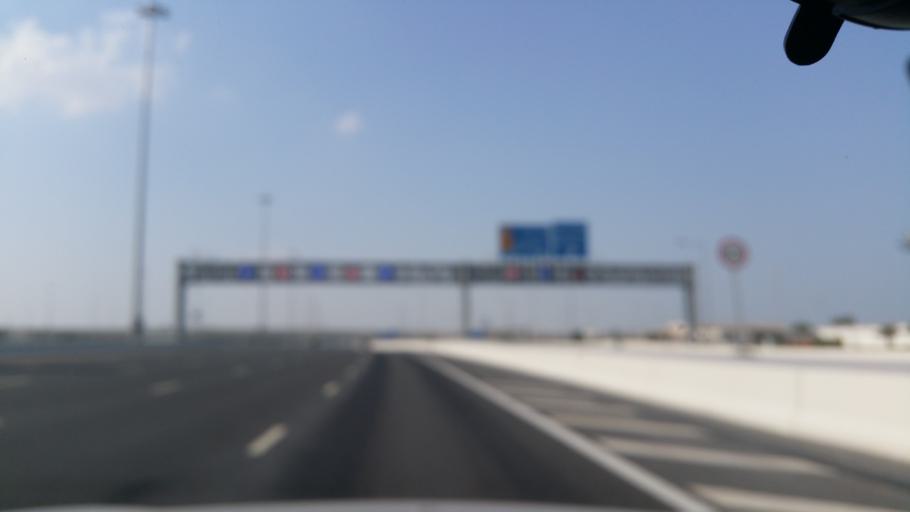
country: QA
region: Baladiyat Umm Salal
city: Umm Salal Muhammad
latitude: 25.3891
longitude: 51.4993
